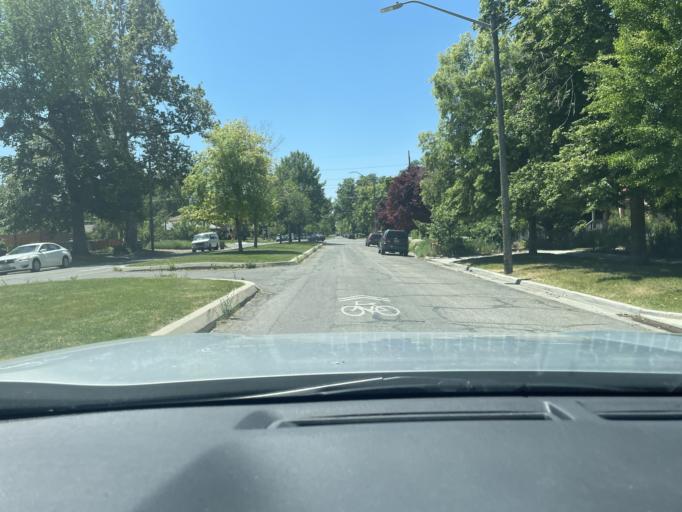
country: US
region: Utah
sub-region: Salt Lake County
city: Salt Lake City
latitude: 40.7529
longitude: -111.8740
